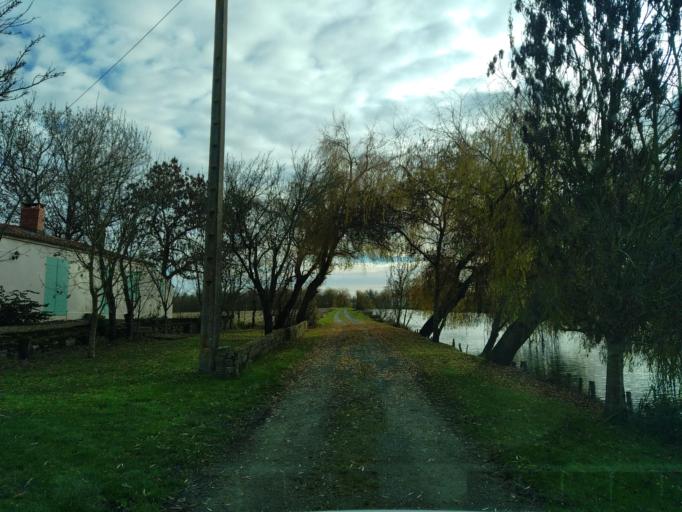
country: FR
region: Pays de la Loire
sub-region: Departement de la Vendee
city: Vix
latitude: 46.3284
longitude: -0.8056
